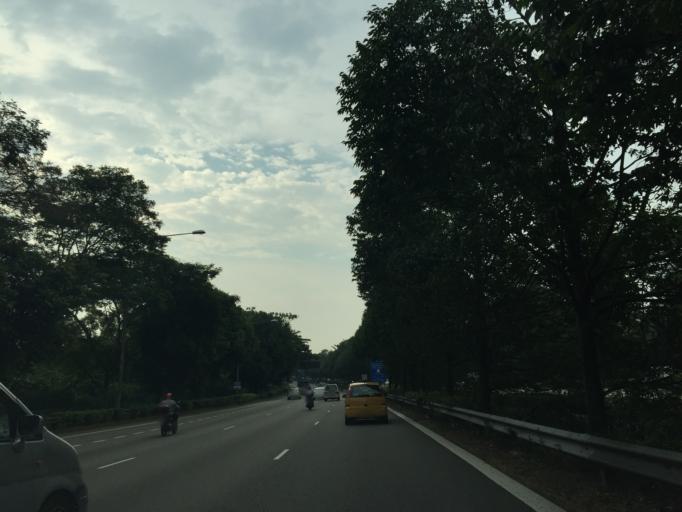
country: MY
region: Johor
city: Johor Bahru
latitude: 1.4240
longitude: 103.7711
